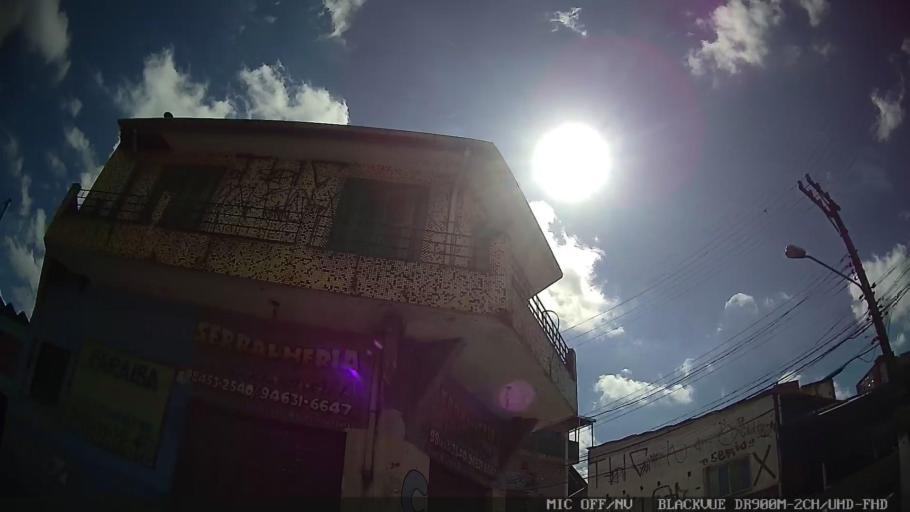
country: BR
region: Sao Paulo
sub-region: Sao Caetano Do Sul
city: Sao Caetano do Sul
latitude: -23.6272
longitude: -46.5912
